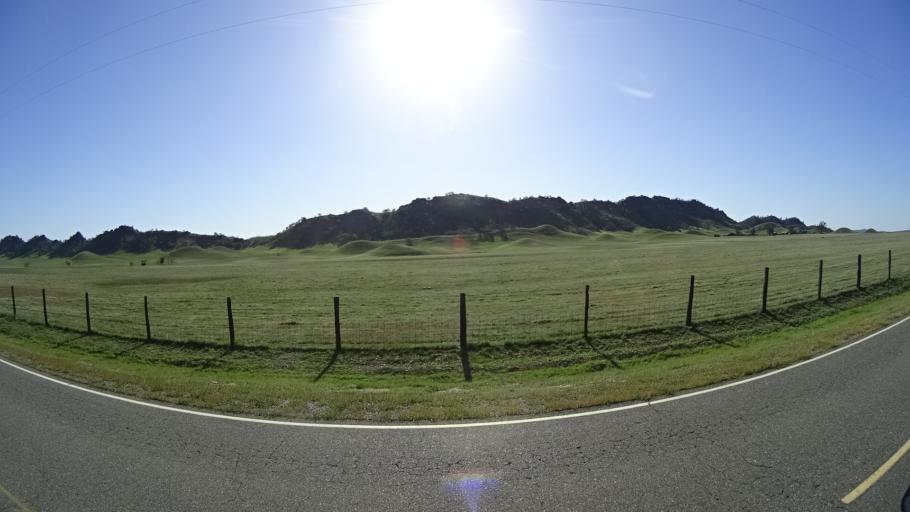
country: US
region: California
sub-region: Tehama County
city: Rancho Tehama Reserve
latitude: 39.7358
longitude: -122.5489
